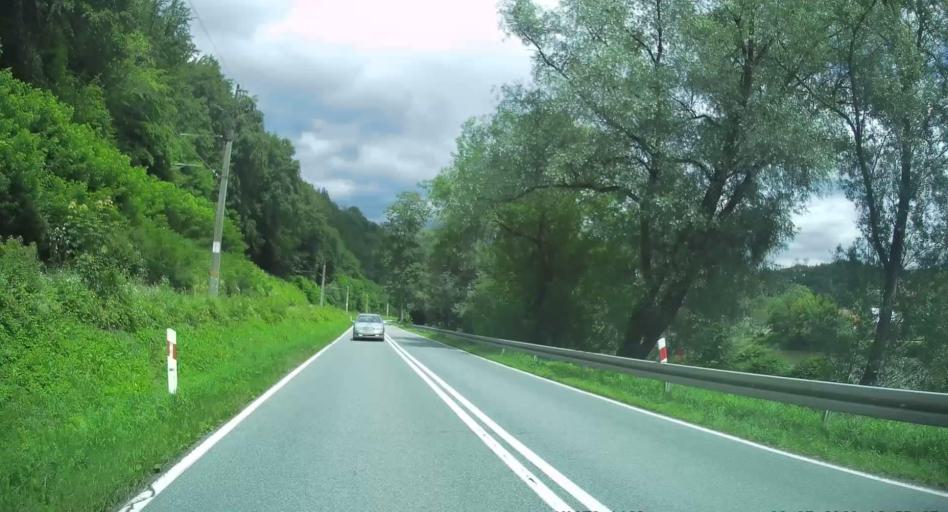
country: PL
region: Lesser Poland Voivodeship
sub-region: Powiat nowosadecki
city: Piwniczna-Zdroj
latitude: 49.3732
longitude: 20.7701
